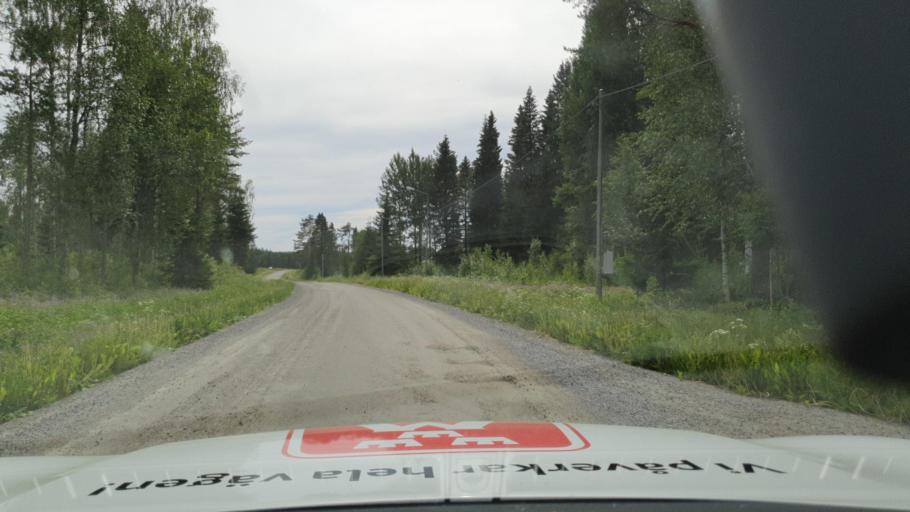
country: SE
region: Vaesterbotten
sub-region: Skelleftea Kommun
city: Burea
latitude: 64.4633
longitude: 21.0416
